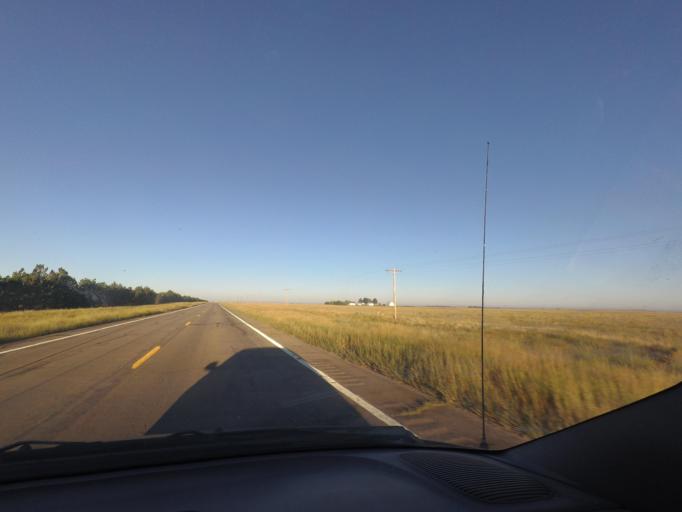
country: US
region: Colorado
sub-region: Yuma County
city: Yuma
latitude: 39.6702
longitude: -102.9000
